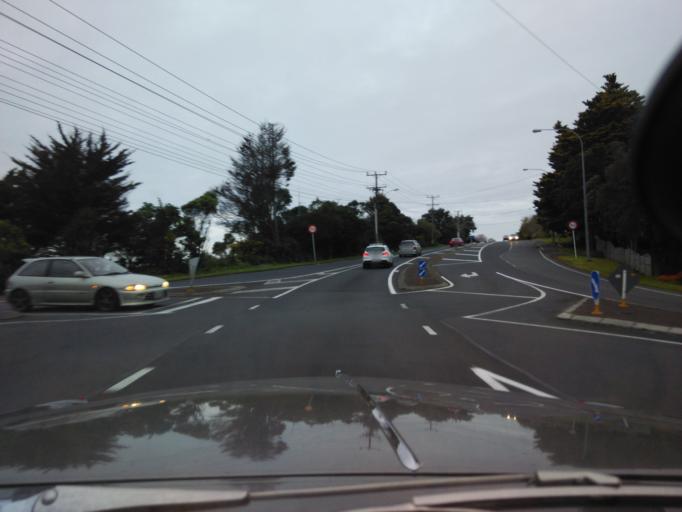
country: NZ
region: Auckland
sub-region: Auckland
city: Rothesay Bay
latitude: -36.7630
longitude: 174.7159
